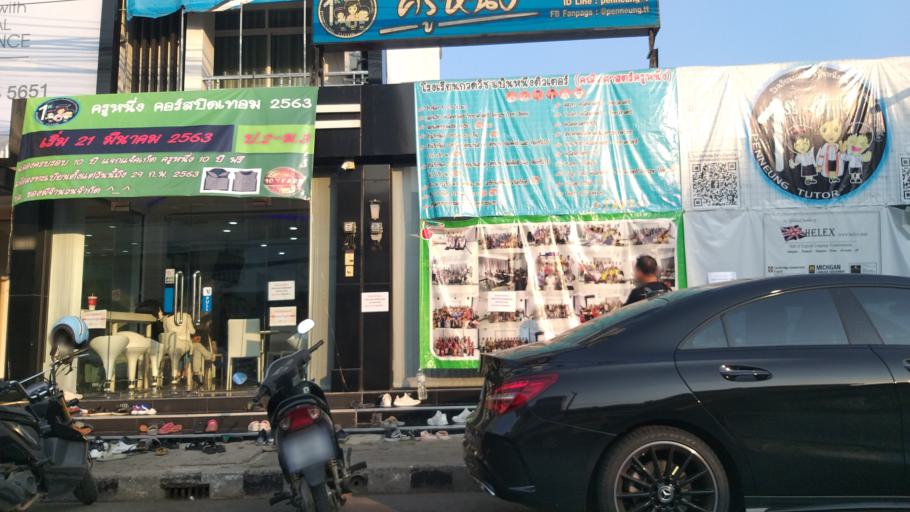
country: TH
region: Khon Kaen
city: Khon Kaen
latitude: 16.4208
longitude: 102.8329
